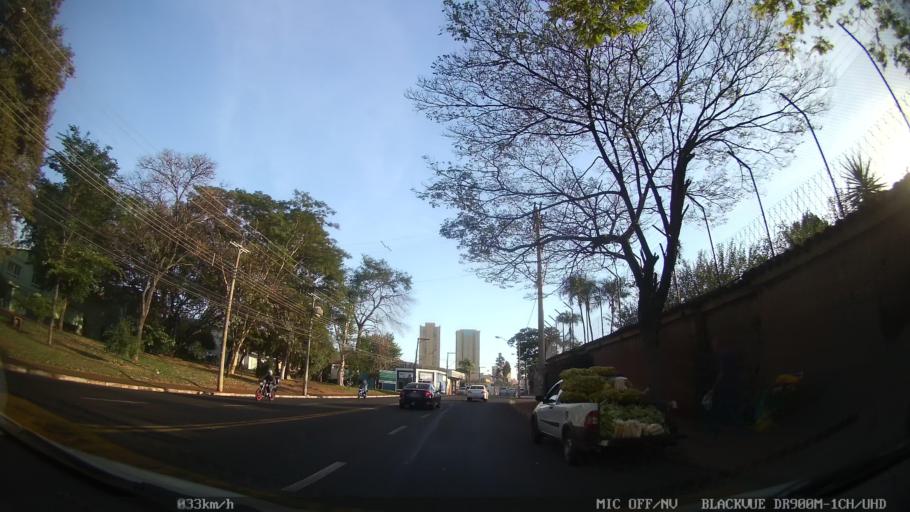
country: BR
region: Sao Paulo
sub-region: Ribeirao Preto
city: Ribeirao Preto
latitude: -21.1983
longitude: -47.8000
